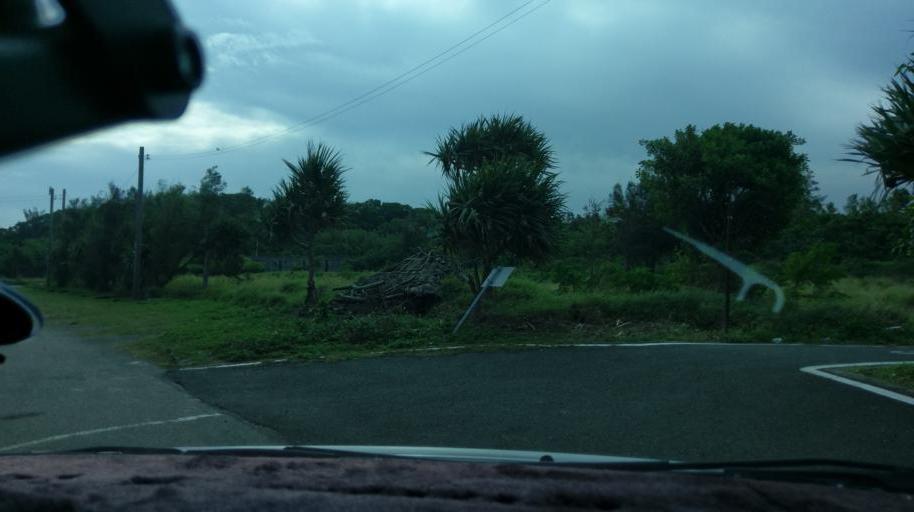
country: TW
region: Taiwan
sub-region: Hsinchu
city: Hsinchu
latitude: 24.7220
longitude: 120.8672
